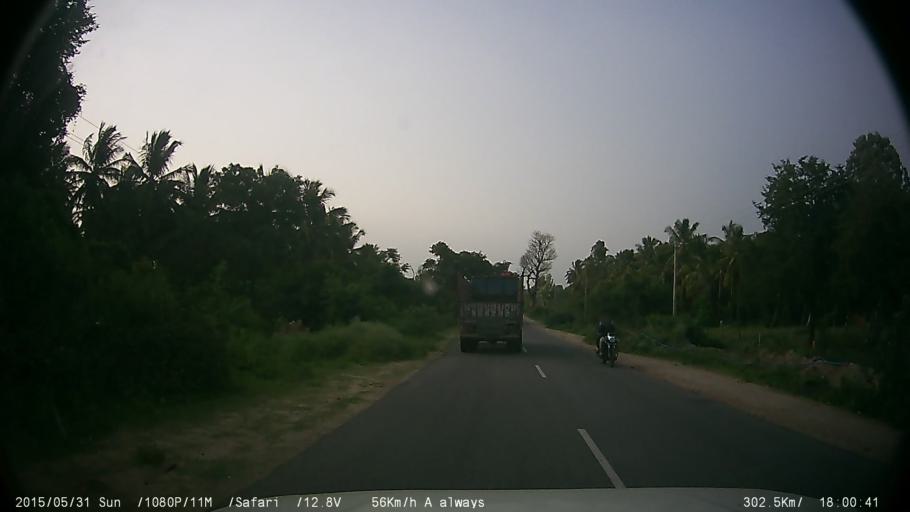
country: IN
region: Karnataka
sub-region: Mysore
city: Nanjangud
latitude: 12.0231
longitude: 76.6731
